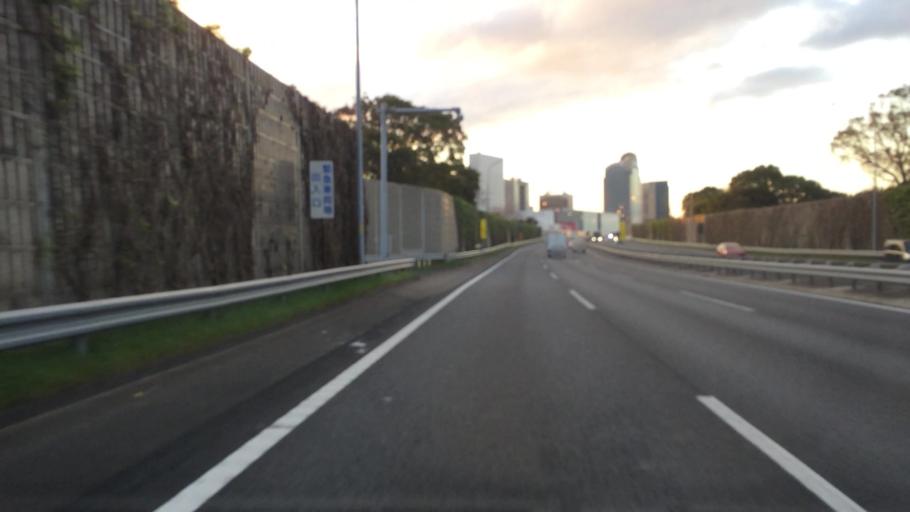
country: JP
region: Chiba
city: Chiba
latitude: 35.6499
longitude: 140.0543
